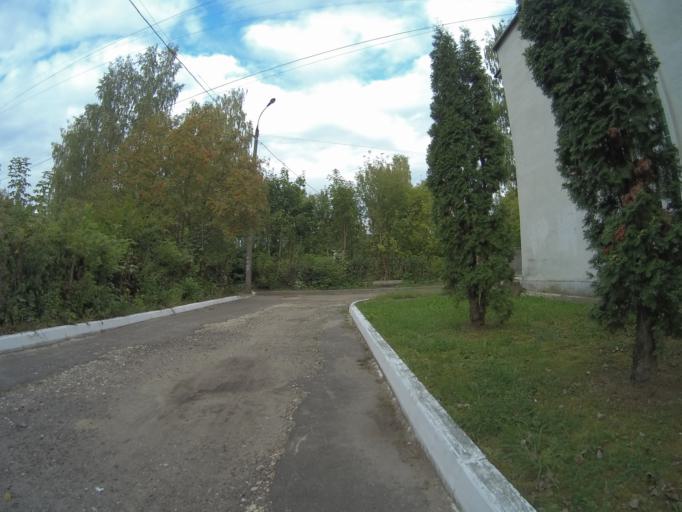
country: RU
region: Vladimir
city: Raduzhnyy
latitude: 56.1037
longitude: 40.2810
